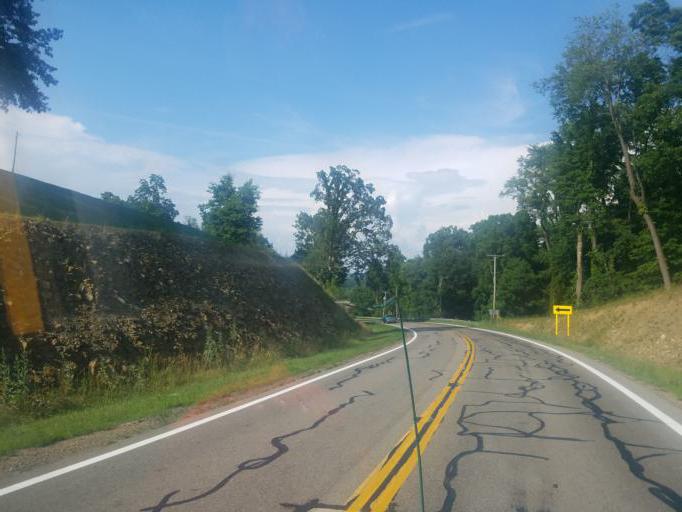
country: US
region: Ohio
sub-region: Wayne County
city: Shreve
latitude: 40.7055
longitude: -82.0921
